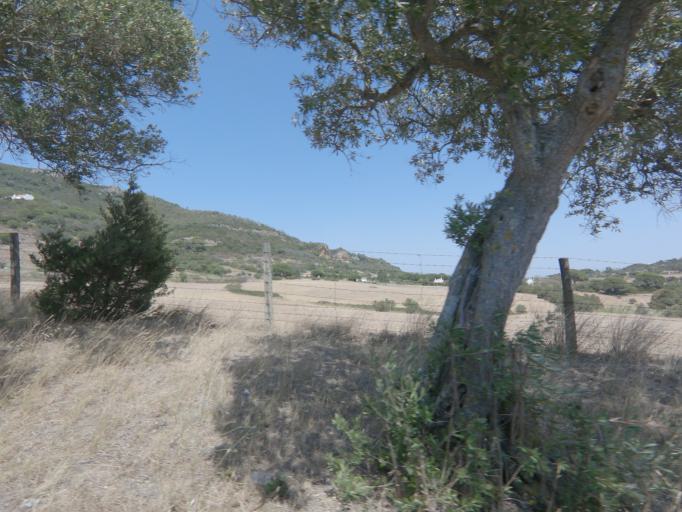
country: PT
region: Setubal
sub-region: Setubal
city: Setubal
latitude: 38.5244
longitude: -8.9323
